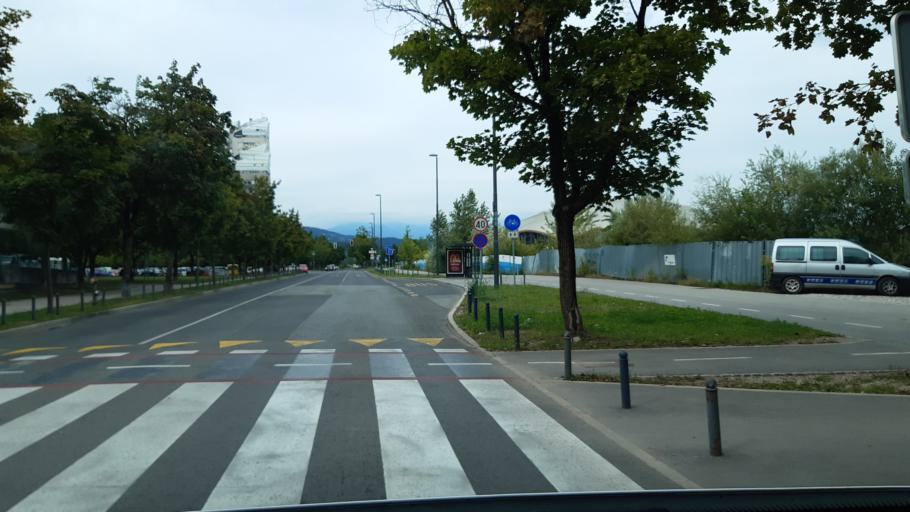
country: SI
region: Ljubljana
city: Ljubljana
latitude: 46.0787
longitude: 14.5198
